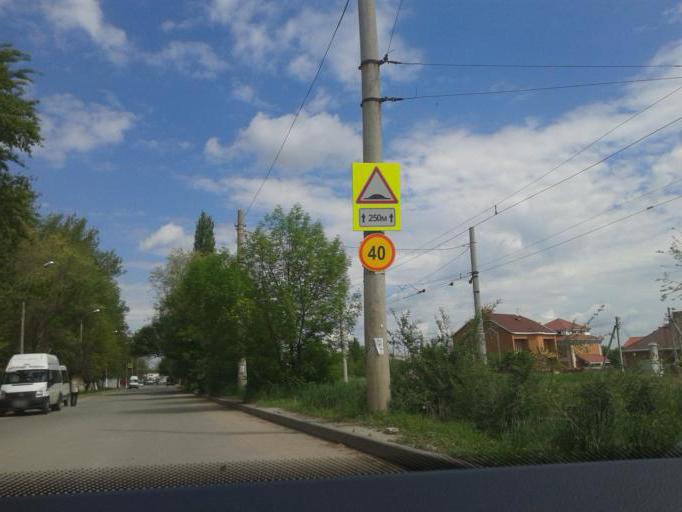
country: RU
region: Volgograd
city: Gorodishche
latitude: 48.7686
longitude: 44.5043
